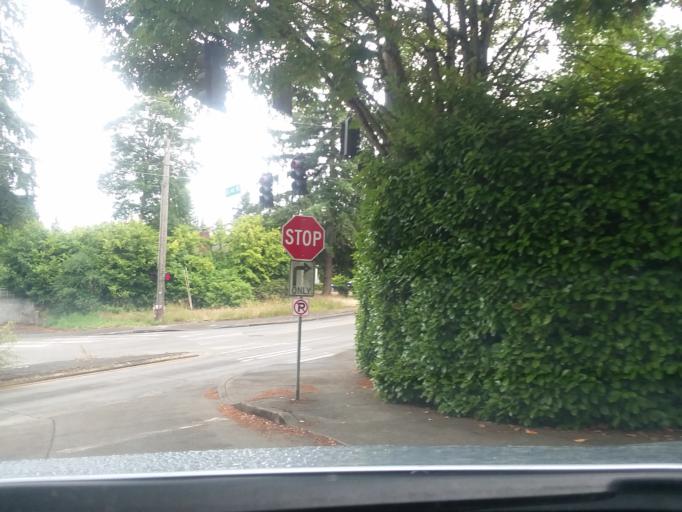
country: US
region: Washington
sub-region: King County
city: Lake Forest Park
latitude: 47.7093
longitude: -122.3035
